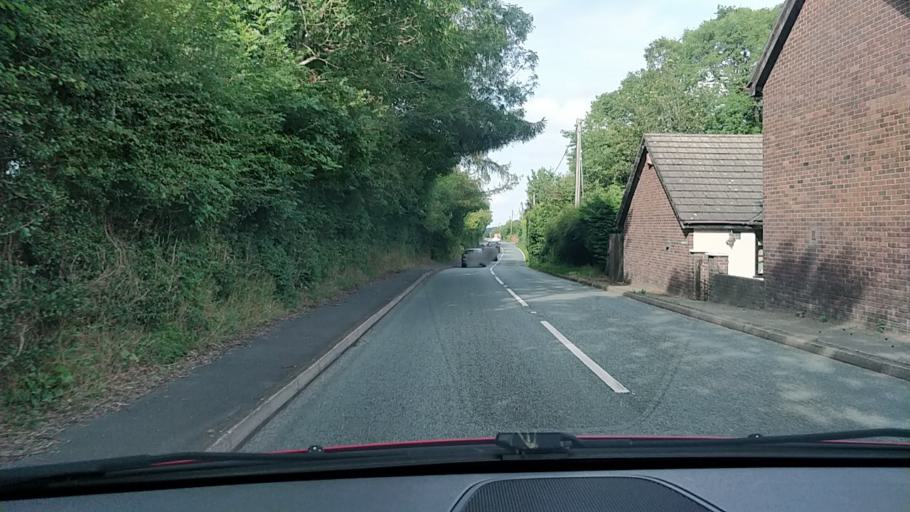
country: GB
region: Wales
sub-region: County of Flintshire
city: Leeswood
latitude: 53.1115
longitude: -3.1186
